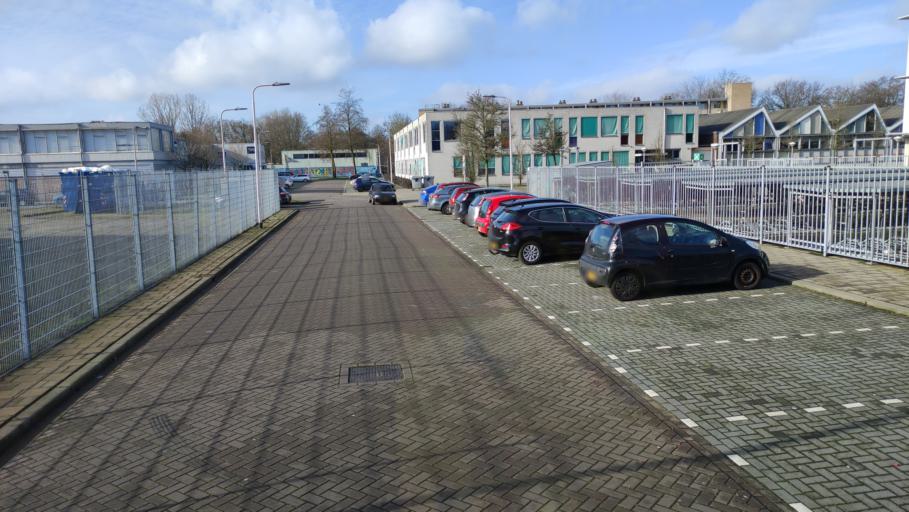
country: NL
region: North Brabant
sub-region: Gemeente Tilburg
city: Tilburg
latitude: 51.5654
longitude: 5.0602
